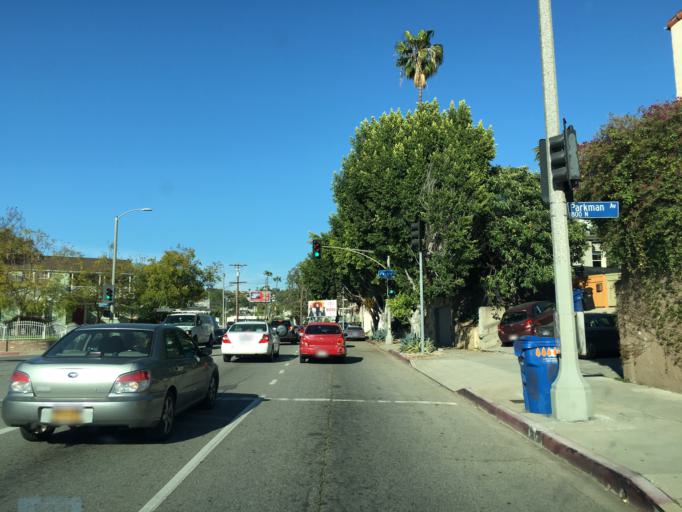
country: US
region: California
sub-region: Los Angeles County
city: Silver Lake
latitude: 34.0812
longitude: -118.2743
